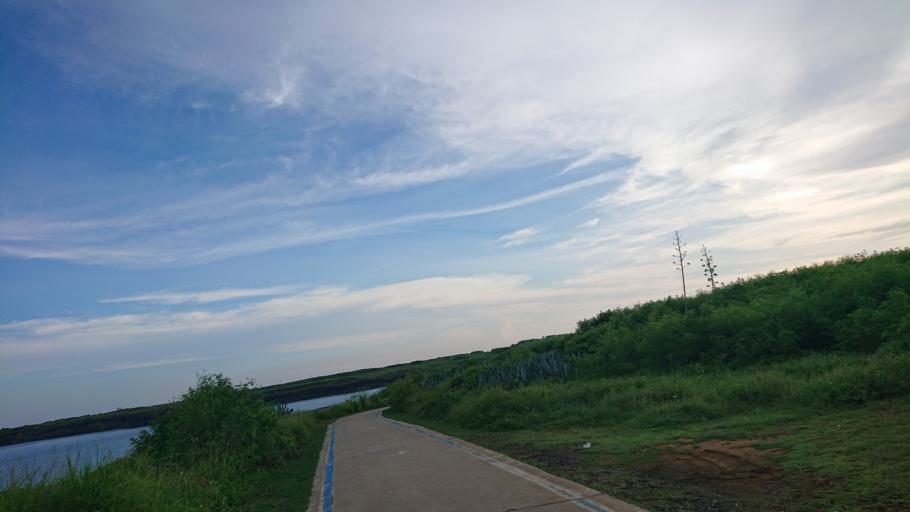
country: TW
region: Taiwan
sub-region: Penghu
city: Ma-kung
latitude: 23.5187
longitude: 119.6091
